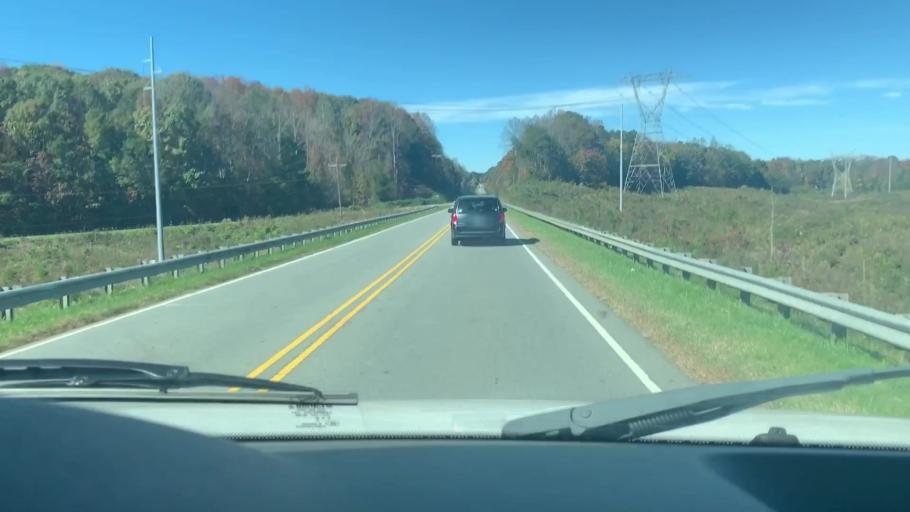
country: US
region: North Carolina
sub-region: Lincoln County
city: Lowesville
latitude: 35.4295
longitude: -80.9636
